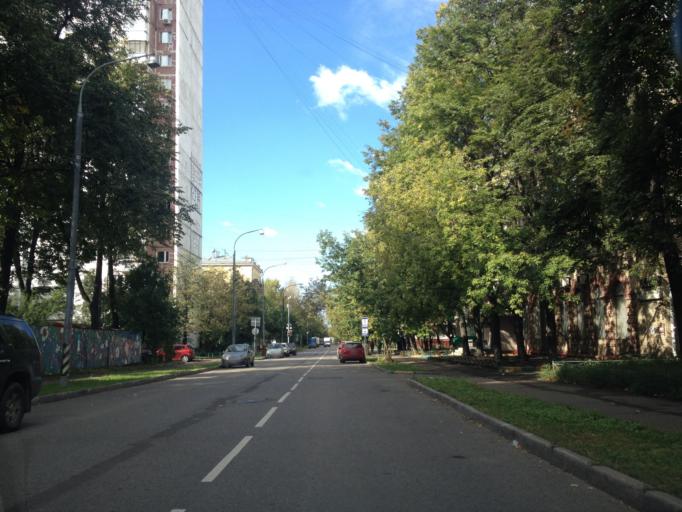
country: RU
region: Moscow
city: Metrogorodok
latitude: 55.7992
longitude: 37.7956
